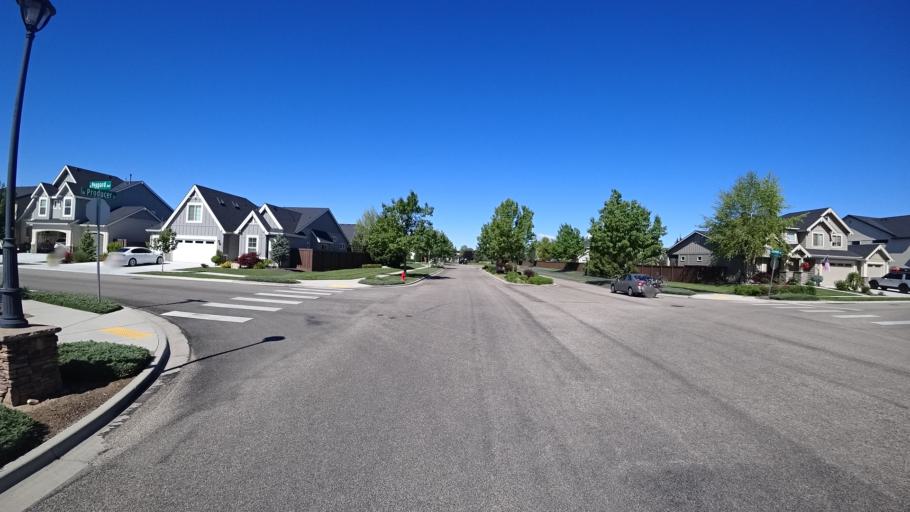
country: US
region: Idaho
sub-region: Ada County
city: Meridian
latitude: 43.6553
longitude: -116.3952
